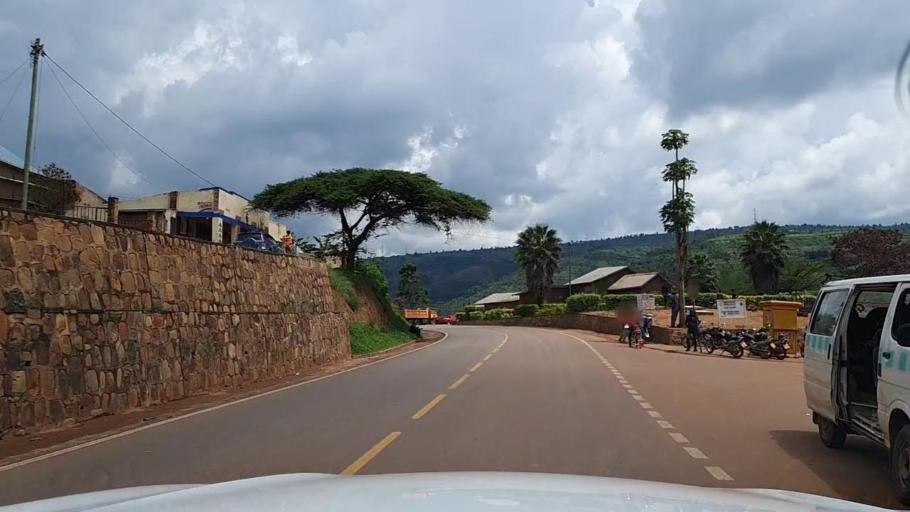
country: RW
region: Kigali
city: Kigali
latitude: -1.8082
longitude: 30.1249
